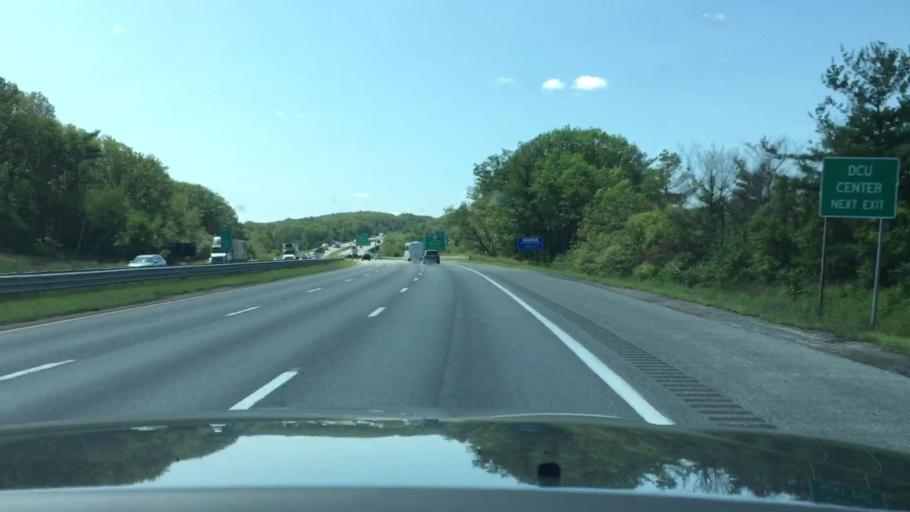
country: US
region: Massachusetts
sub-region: Worcester County
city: Auburn
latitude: 42.2002
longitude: -71.8376
